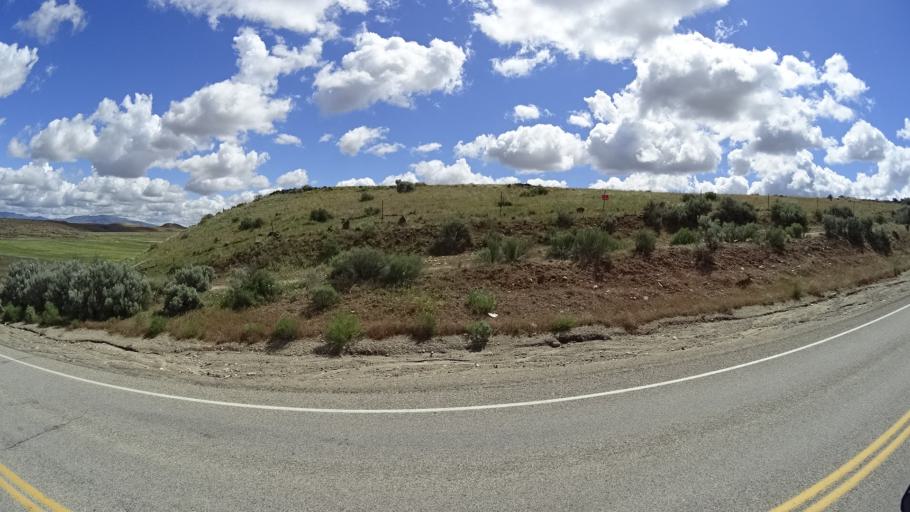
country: US
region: Idaho
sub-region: Ada County
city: Boise
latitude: 43.4853
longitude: -116.2340
